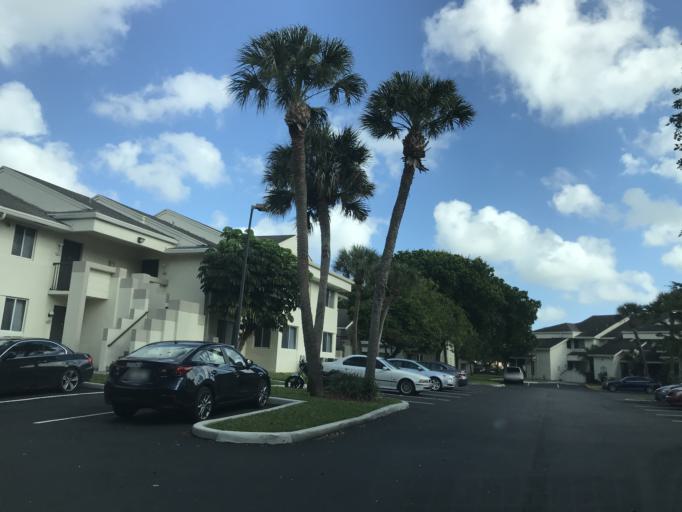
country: US
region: Florida
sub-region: Broward County
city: Coconut Creek
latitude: 26.2697
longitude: -80.1935
